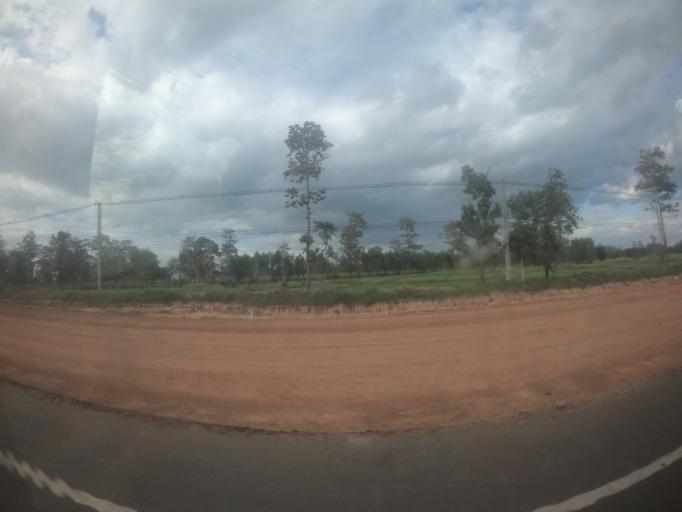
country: TH
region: Surin
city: Kap Choeng
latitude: 14.5116
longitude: 103.5515
